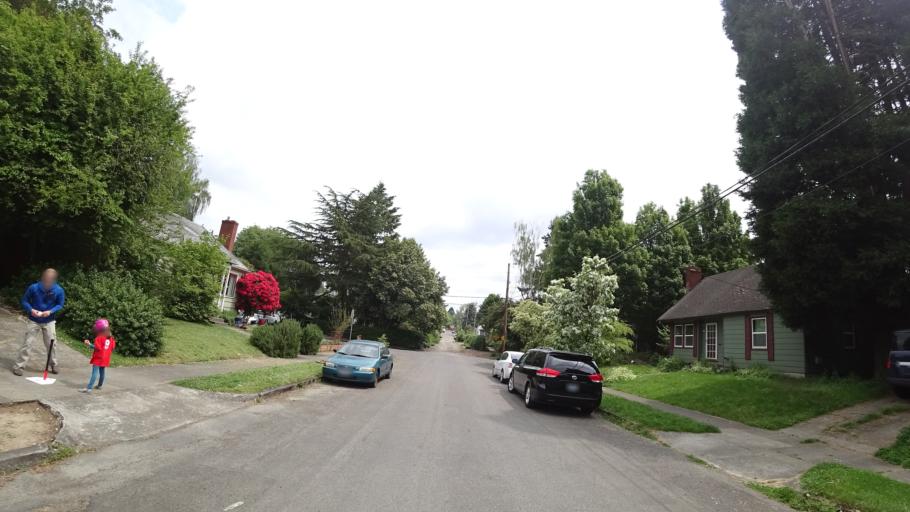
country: US
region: Oregon
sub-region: Clackamas County
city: Milwaukie
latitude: 45.4892
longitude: -122.6272
